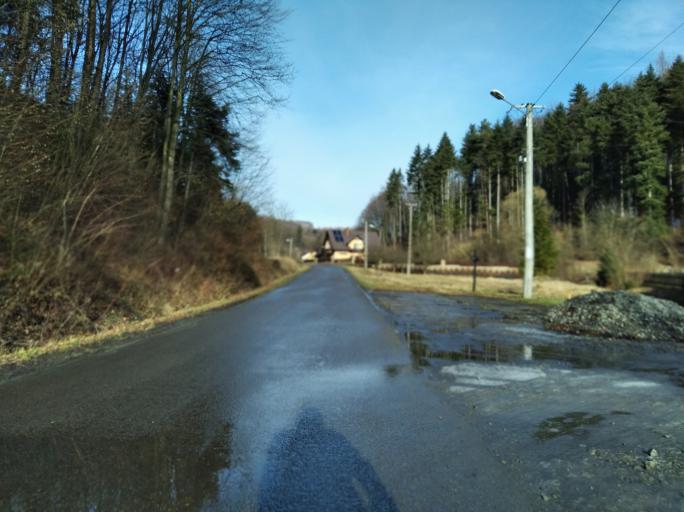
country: PL
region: Subcarpathian Voivodeship
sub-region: Powiat strzyzowski
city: Strzyzow
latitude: 49.8858
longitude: 21.7750
